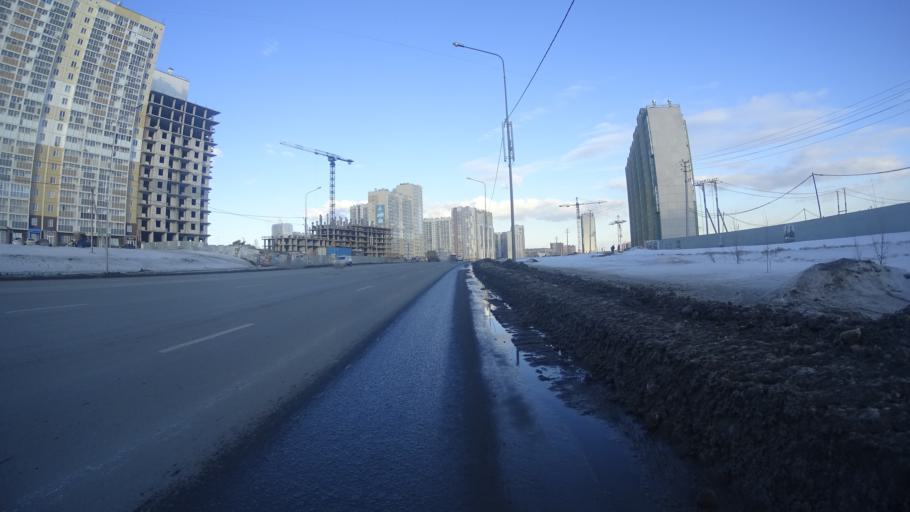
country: RU
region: Chelyabinsk
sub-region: Gorod Chelyabinsk
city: Chelyabinsk
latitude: 55.1738
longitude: 61.3185
